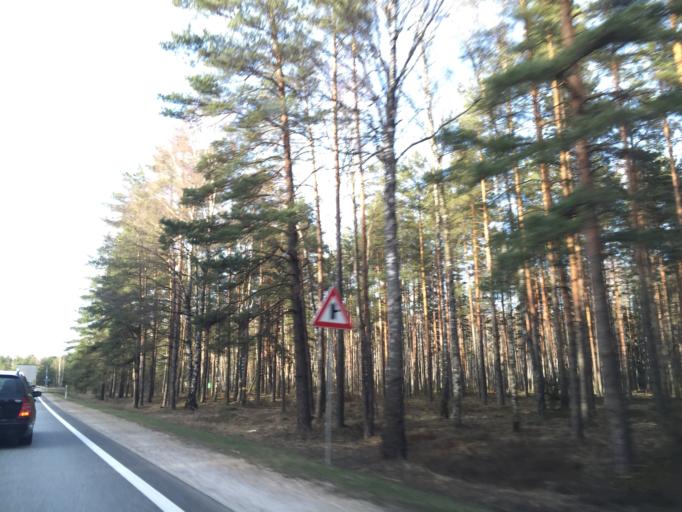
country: LV
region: Riga
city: Bergi
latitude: 56.9547
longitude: 24.3774
